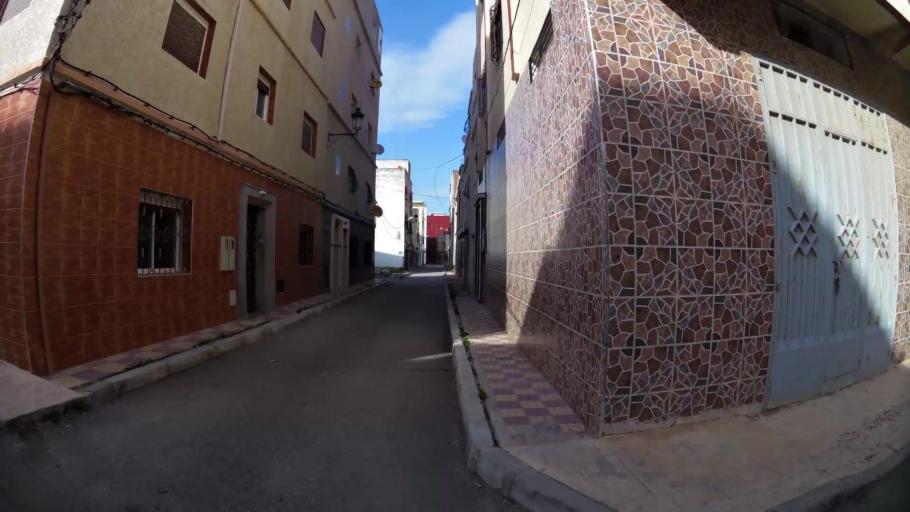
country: MA
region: Tanger-Tetouan
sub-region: Tetouan
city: Martil
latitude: 35.6100
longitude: -5.2822
